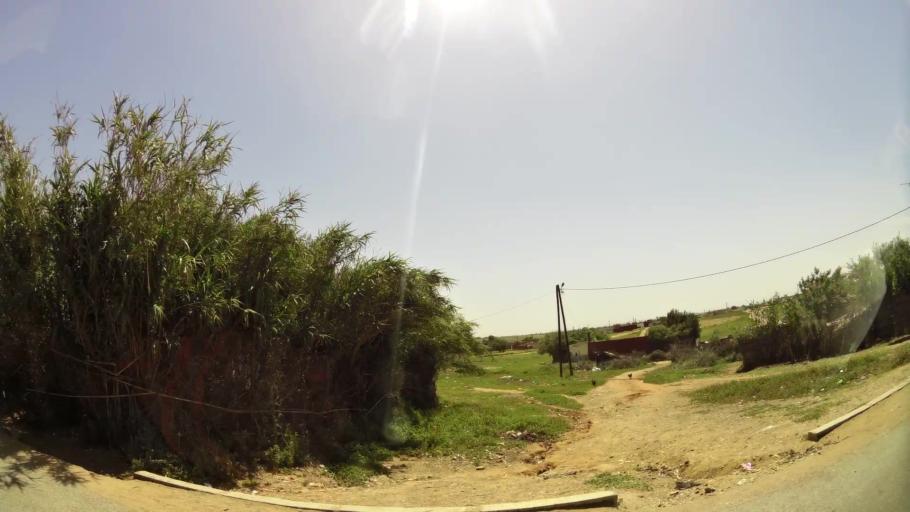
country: MA
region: Rabat-Sale-Zemmour-Zaer
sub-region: Khemisset
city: Khemisset
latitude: 33.8092
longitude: -6.0698
